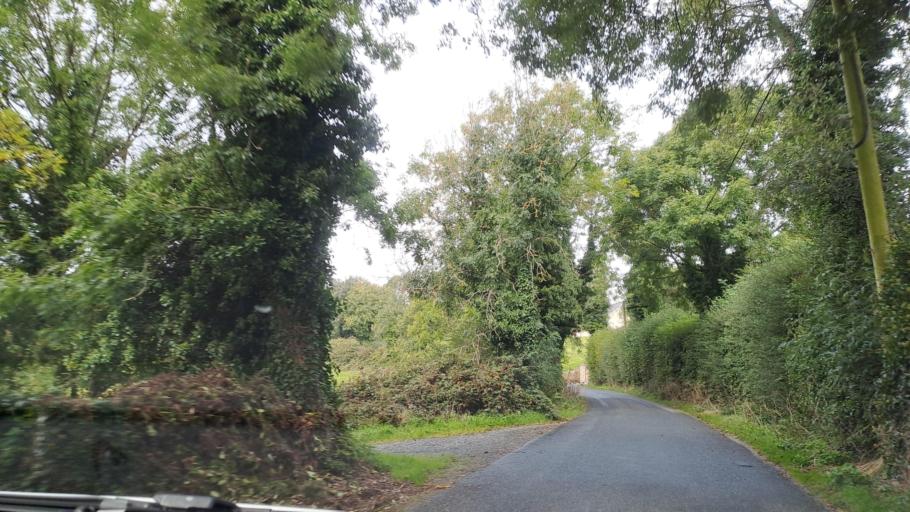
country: IE
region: Ulster
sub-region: County Monaghan
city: Carrickmacross
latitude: 53.9886
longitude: -6.7712
